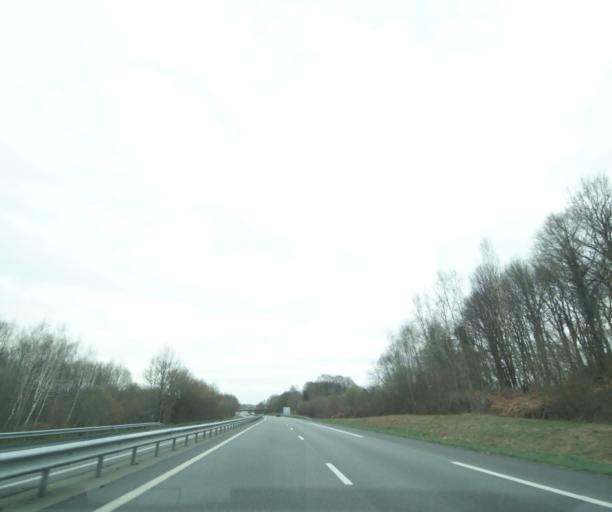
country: FR
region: Limousin
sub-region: Departement de la Haute-Vienne
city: Vicq-sur-Breuilh
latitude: 45.6374
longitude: 1.4238
